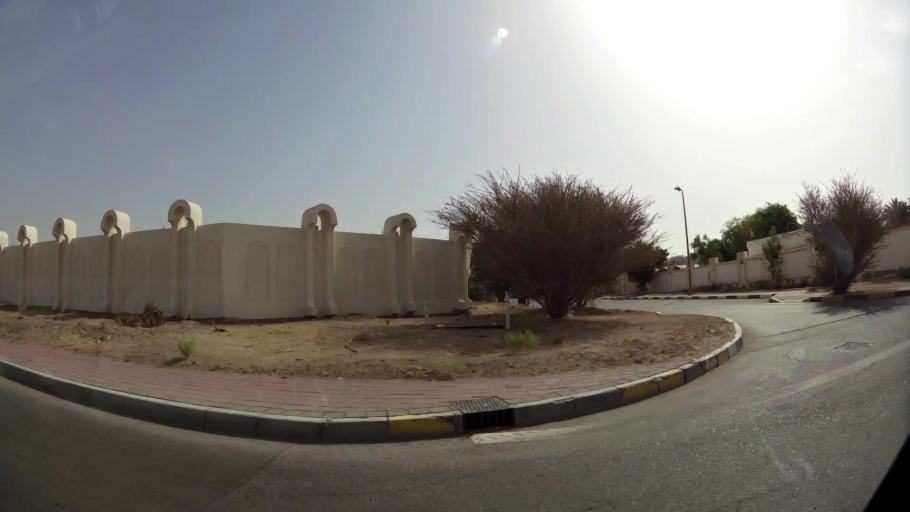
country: AE
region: Abu Dhabi
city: Al Ain
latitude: 24.1460
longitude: 55.7031
